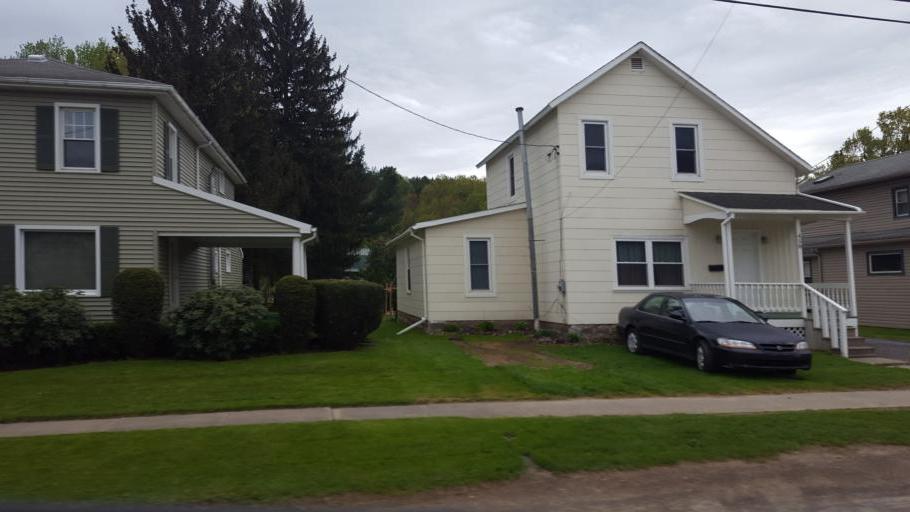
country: US
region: Pennsylvania
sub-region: Tioga County
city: Westfield
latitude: 41.9222
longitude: -77.5311
